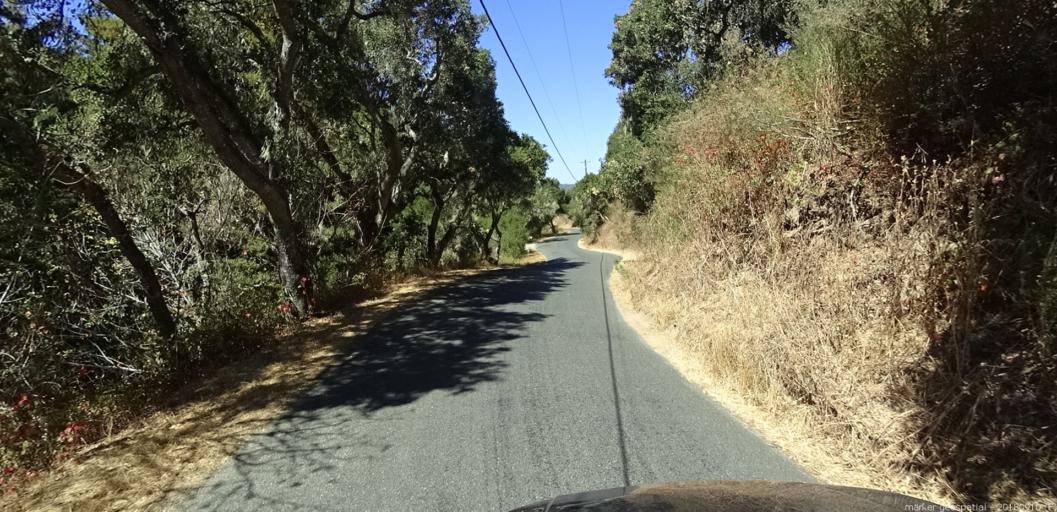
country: US
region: California
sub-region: Monterey County
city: Carmel Valley Village
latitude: 36.5081
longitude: -121.8090
